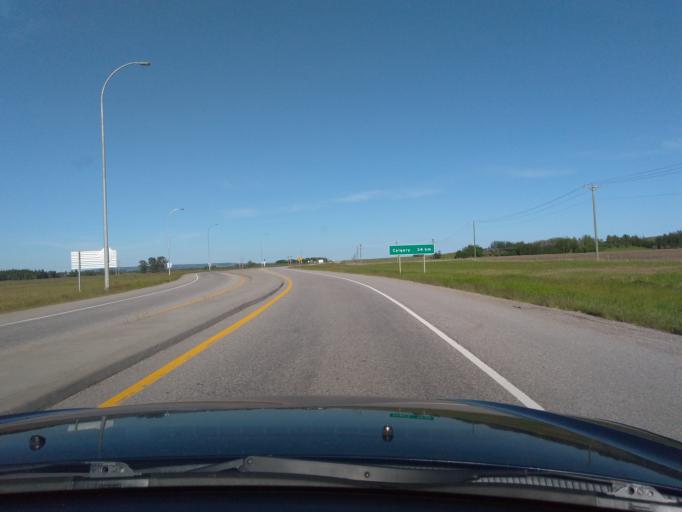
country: CA
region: Alberta
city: Cochrane
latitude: 51.0233
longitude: -114.4646
